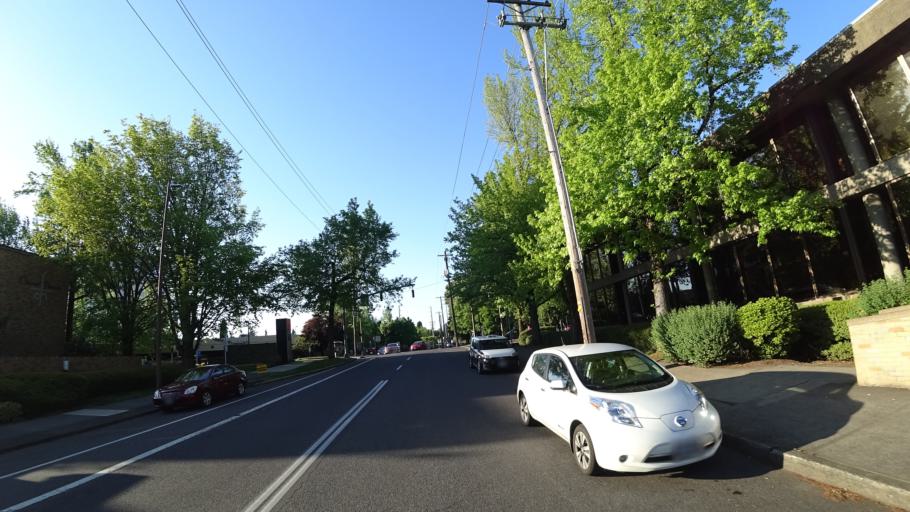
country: US
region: Oregon
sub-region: Multnomah County
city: Portland
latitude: 45.5434
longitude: -122.6681
